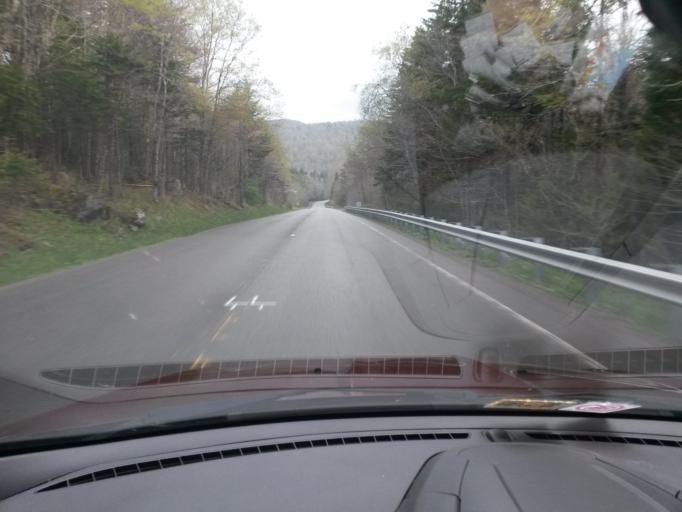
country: US
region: West Virginia
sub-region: Randolph County
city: Elkins
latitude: 38.6116
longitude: -79.8671
